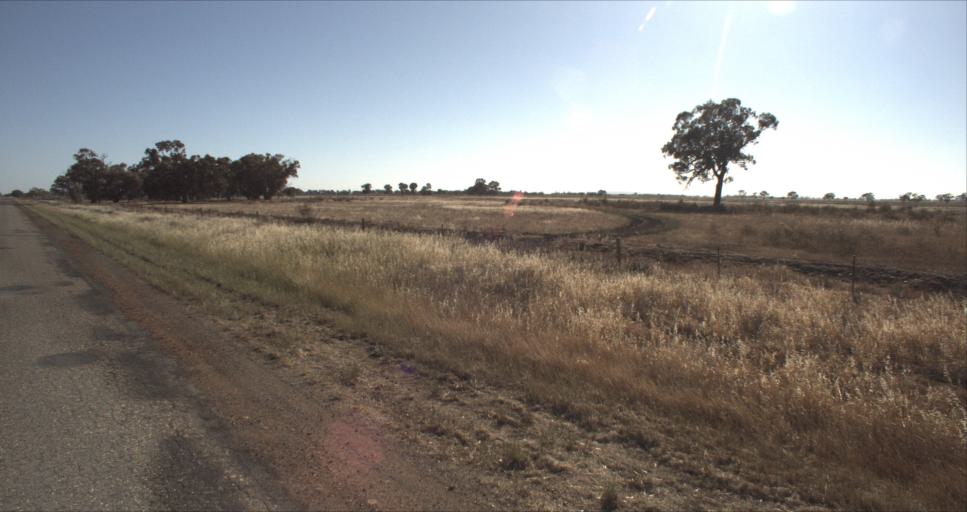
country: AU
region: New South Wales
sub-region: Leeton
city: Leeton
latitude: -34.5917
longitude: 146.2595
